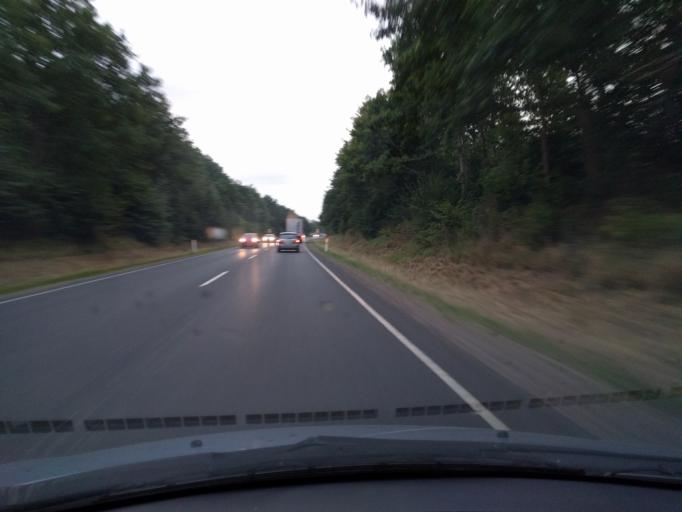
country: DK
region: South Denmark
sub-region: Odense Kommune
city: Bellinge
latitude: 55.3499
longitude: 10.3325
